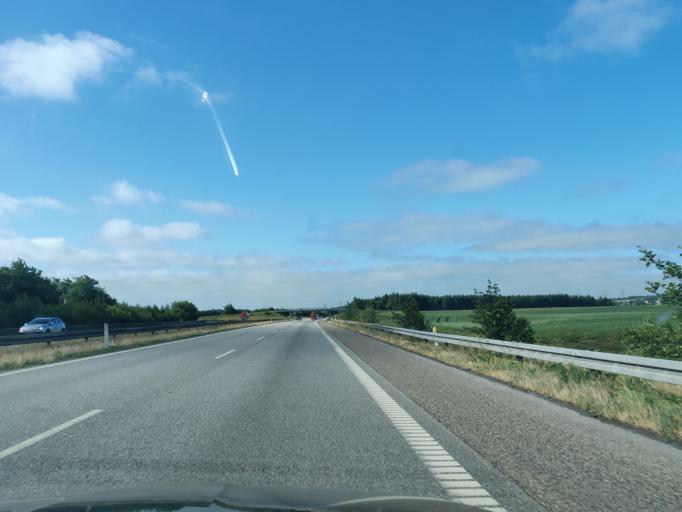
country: DK
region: North Denmark
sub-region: Alborg Kommune
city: Svenstrup
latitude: 56.9689
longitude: 9.8771
